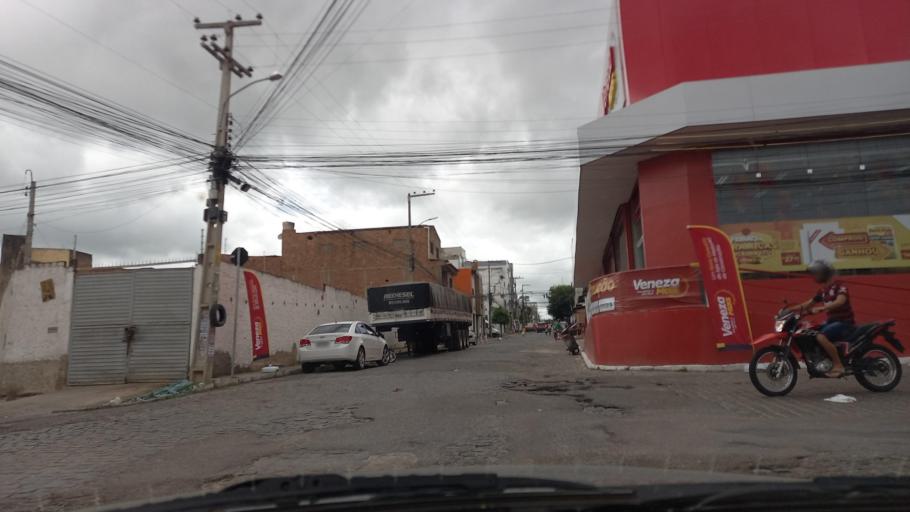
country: BR
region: Pernambuco
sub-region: Caruaru
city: Caruaru
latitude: -8.2735
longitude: -35.9610
